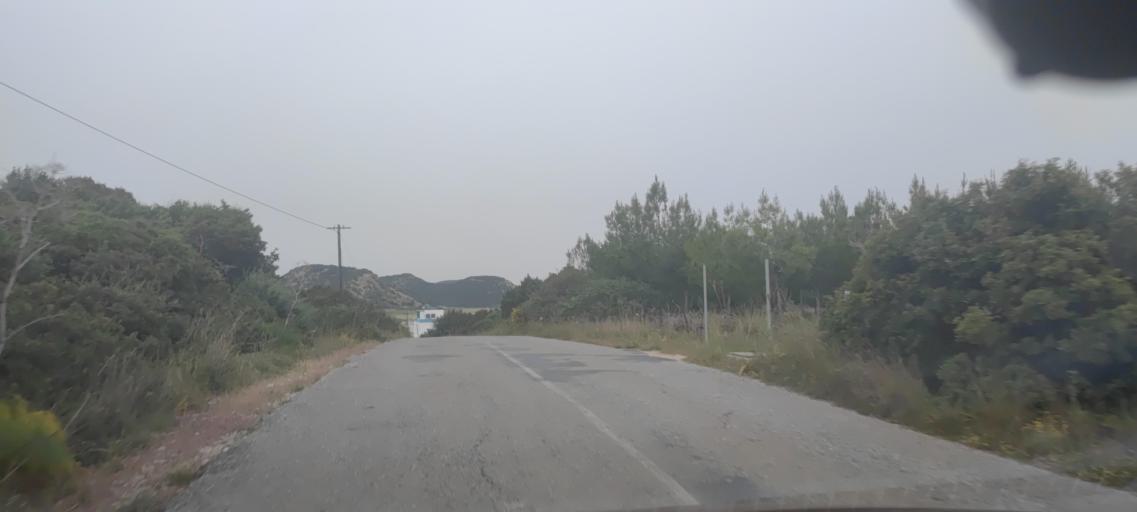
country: CY
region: Ammochostos
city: Rizokarpaso
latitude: 35.5986
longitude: 34.4329
